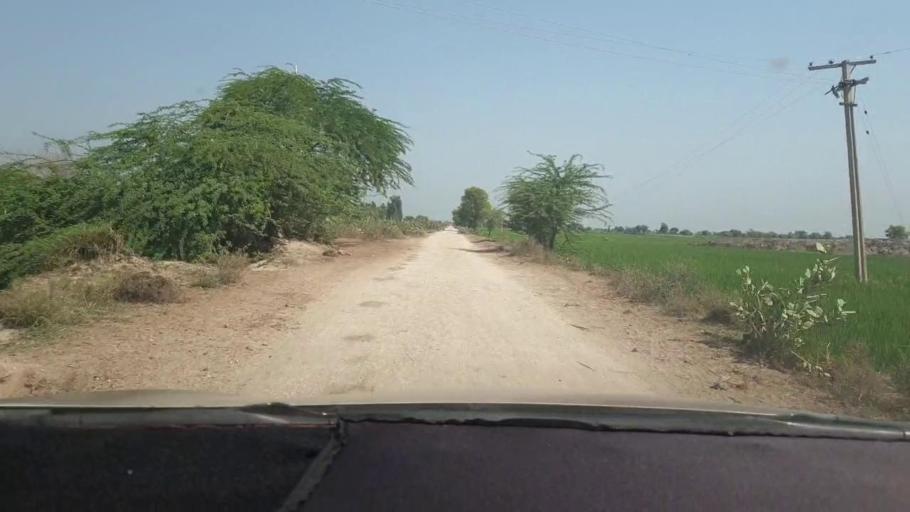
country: PK
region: Sindh
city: Miro Khan
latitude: 27.6743
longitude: 68.1364
